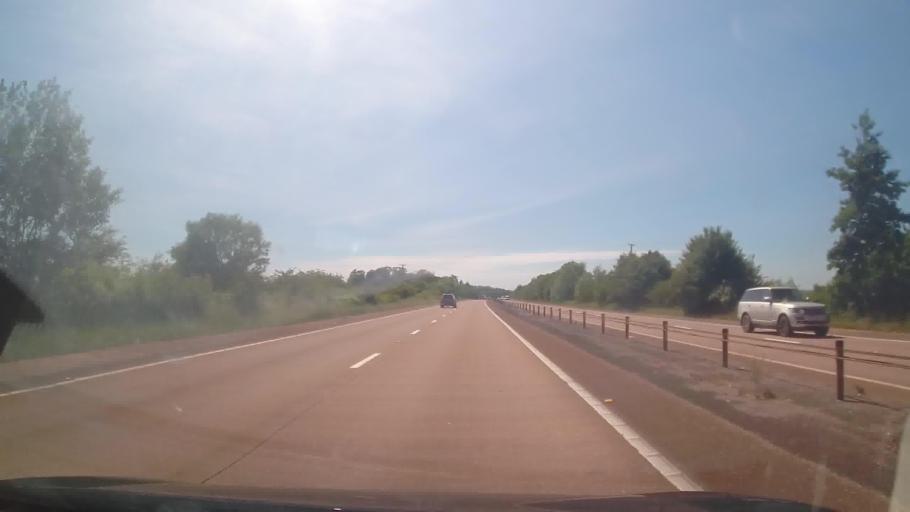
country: GB
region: England
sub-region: Devon
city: Topsham
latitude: 50.7291
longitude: -3.3967
